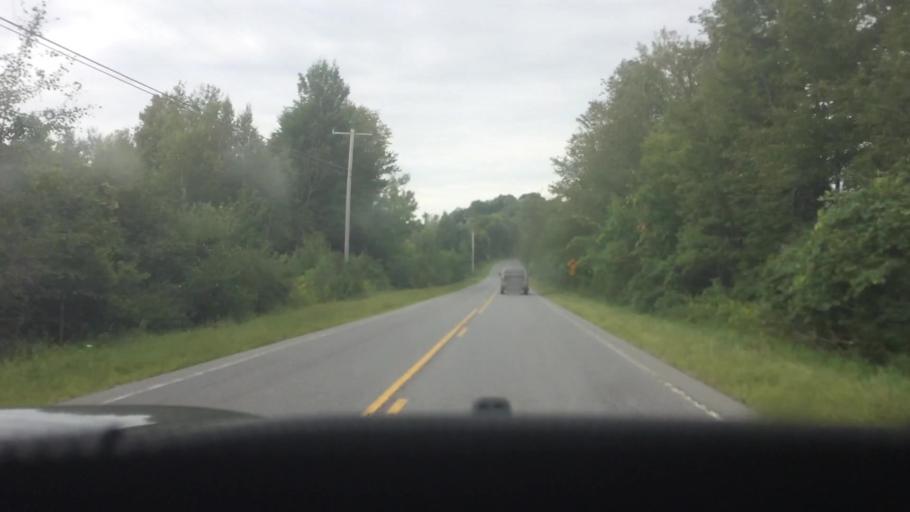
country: US
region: New York
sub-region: St. Lawrence County
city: Canton
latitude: 44.4807
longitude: -75.2234
